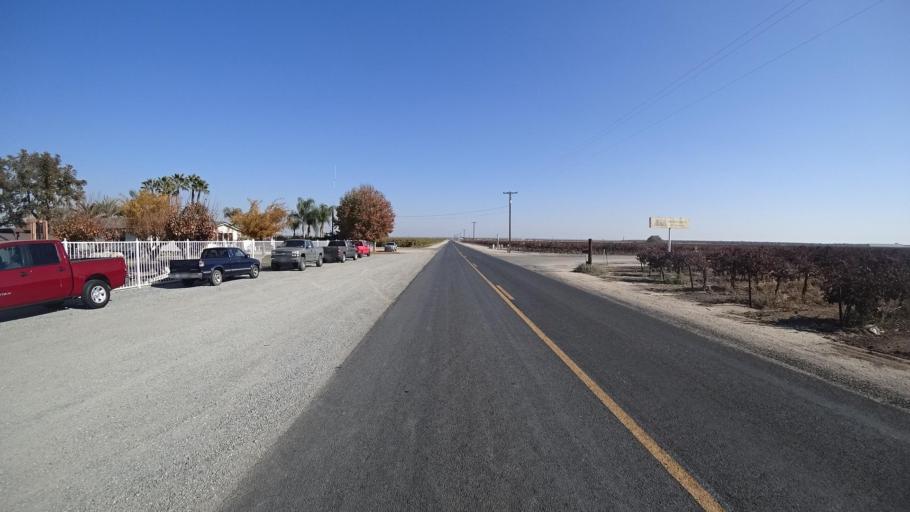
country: US
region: California
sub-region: Kern County
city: McFarland
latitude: 35.6455
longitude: -119.2143
